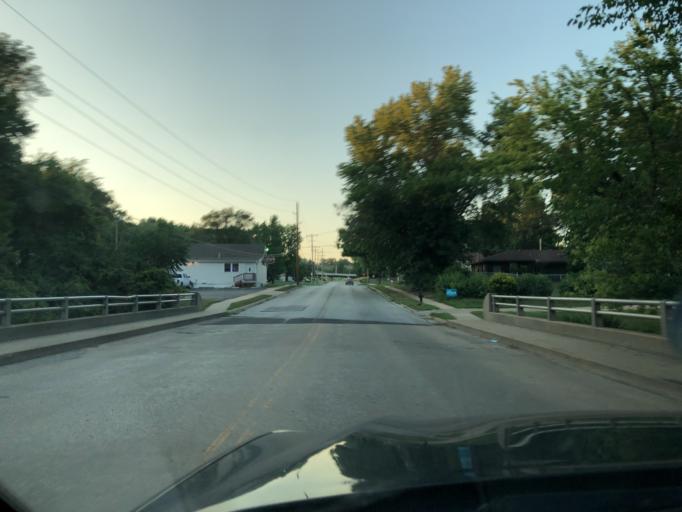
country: US
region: Kansas
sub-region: Leavenworth County
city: Leavenworth
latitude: 39.3244
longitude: -94.9506
